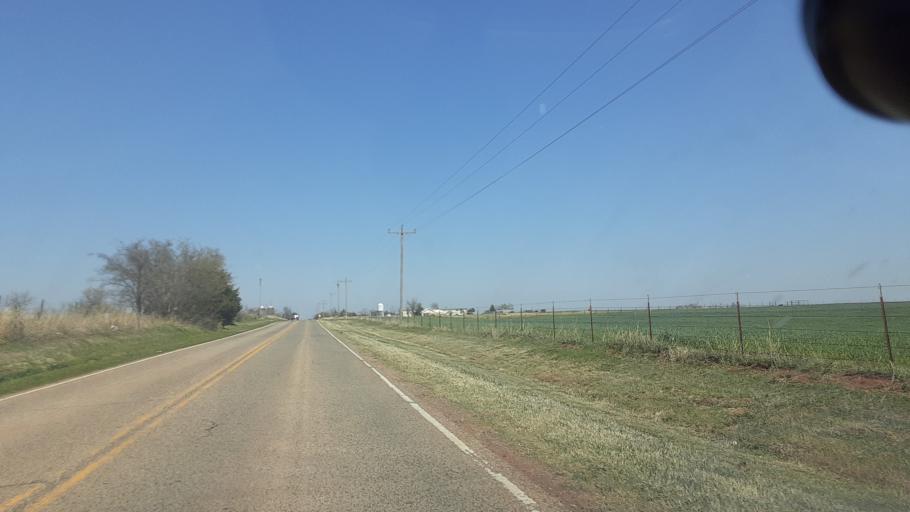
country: US
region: Oklahoma
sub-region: Logan County
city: Guthrie
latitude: 35.8333
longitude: -97.4787
